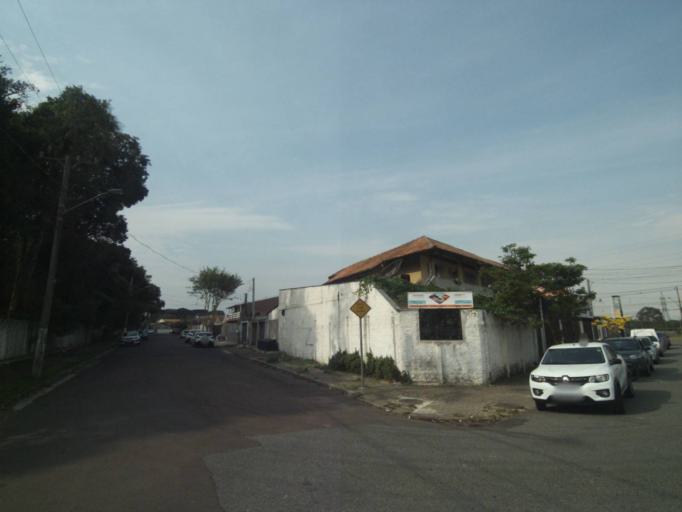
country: BR
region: Parana
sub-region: Sao Jose Dos Pinhais
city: Sao Jose dos Pinhais
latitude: -25.4948
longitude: -49.2092
